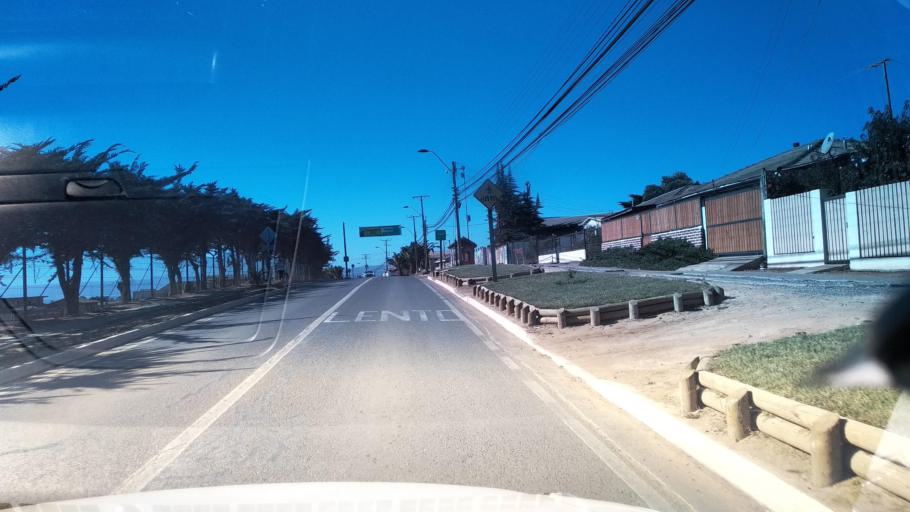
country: CL
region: O'Higgins
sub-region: Provincia de Colchagua
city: Santa Cruz
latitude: -34.3944
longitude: -72.0173
